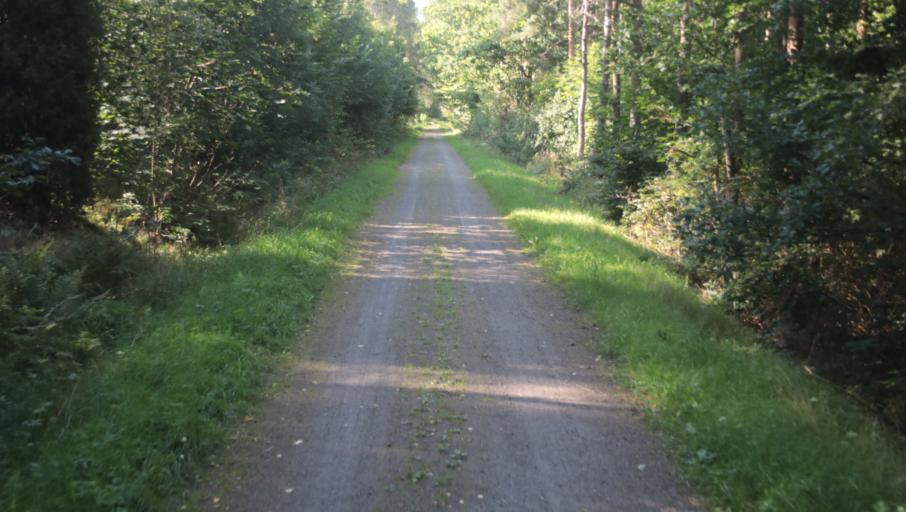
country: SE
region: Blekinge
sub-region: Karlshamns Kommun
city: Svangsta
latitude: 56.2874
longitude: 14.7492
